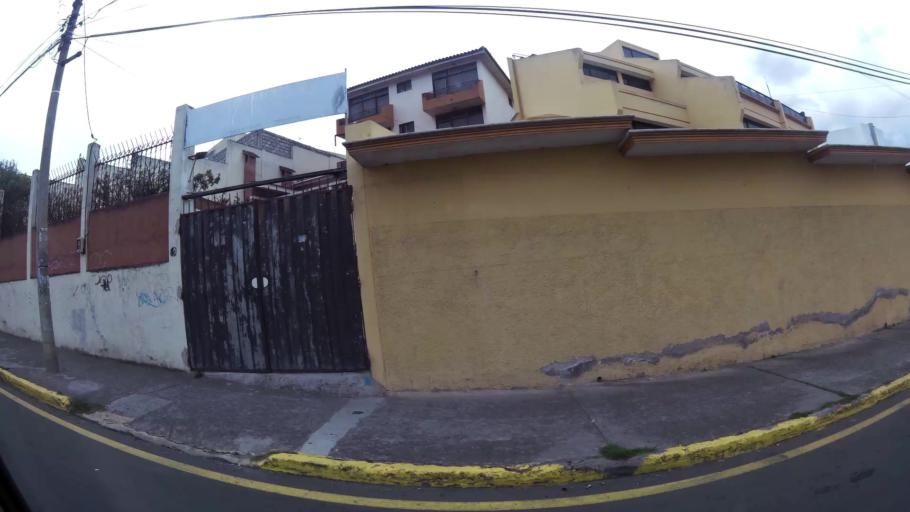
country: EC
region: Tungurahua
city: Ambato
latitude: -1.2598
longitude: -78.6297
